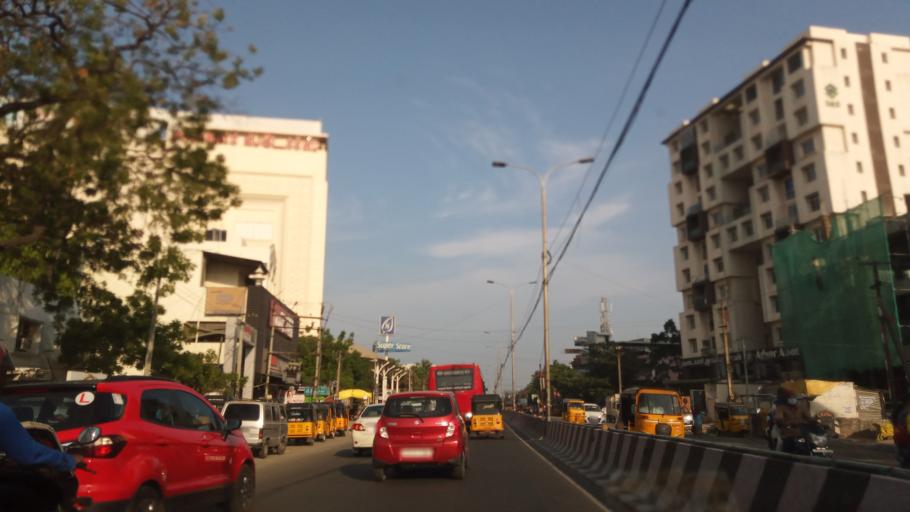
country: IN
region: Tamil Nadu
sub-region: Thiruvallur
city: Porur
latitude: 13.0326
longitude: 80.1631
